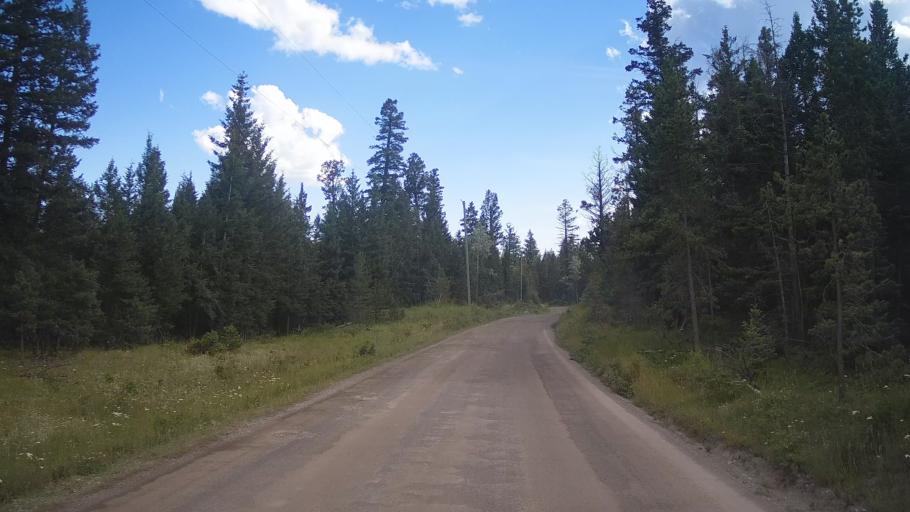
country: CA
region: British Columbia
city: Cache Creek
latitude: 51.1977
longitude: -121.5906
